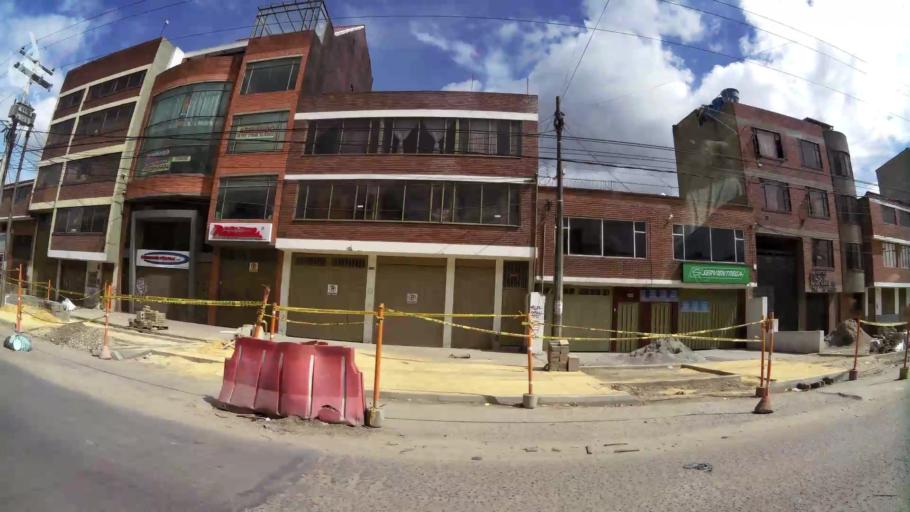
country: CO
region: Bogota D.C.
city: Bogota
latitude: 4.6146
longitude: -74.1338
